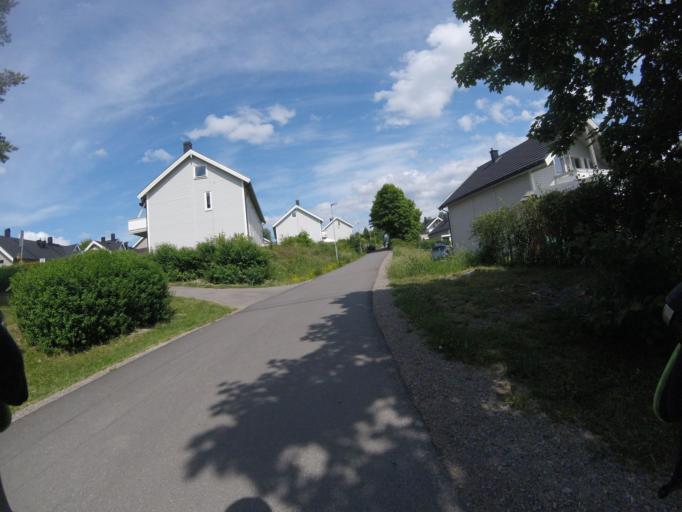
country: NO
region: Akershus
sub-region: Skedsmo
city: Lillestrom
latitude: 59.9897
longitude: 11.0359
